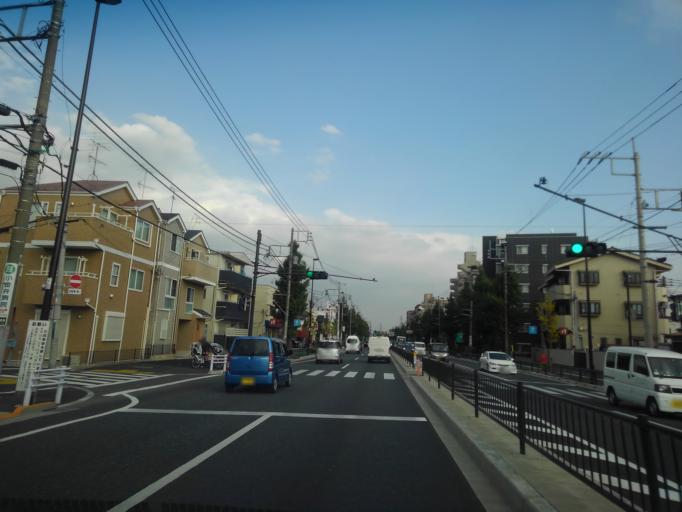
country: JP
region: Tokyo
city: Kokubunji
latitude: 35.6895
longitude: 139.5027
